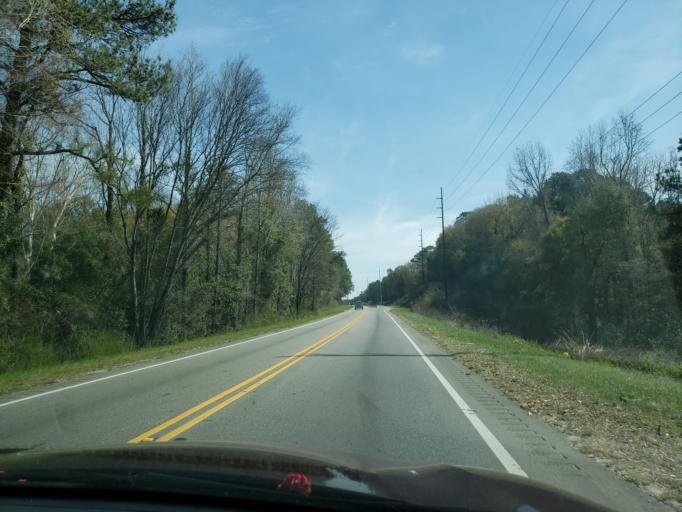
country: US
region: Alabama
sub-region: Autauga County
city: Prattville
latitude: 32.4355
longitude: -86.4614
